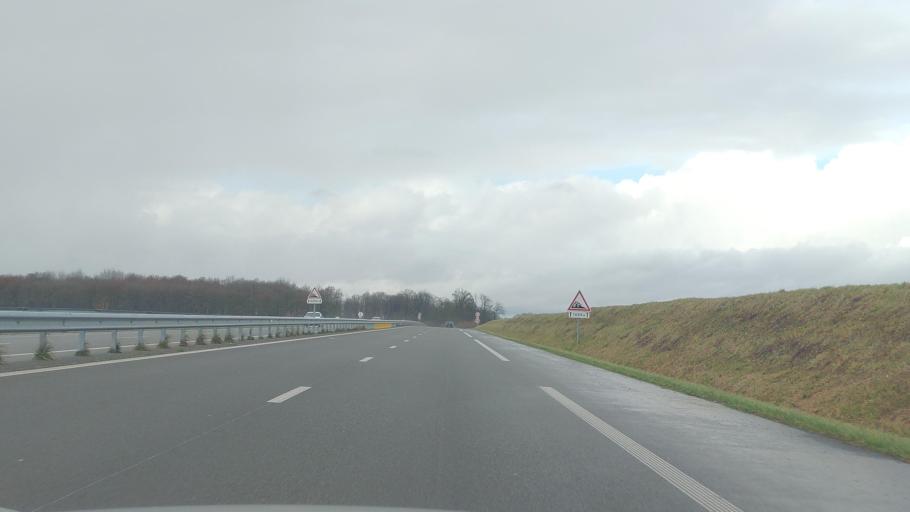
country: FR
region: Picardie
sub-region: Departement de l'Oise
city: Troissereux
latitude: 49.4726
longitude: 2.0721
